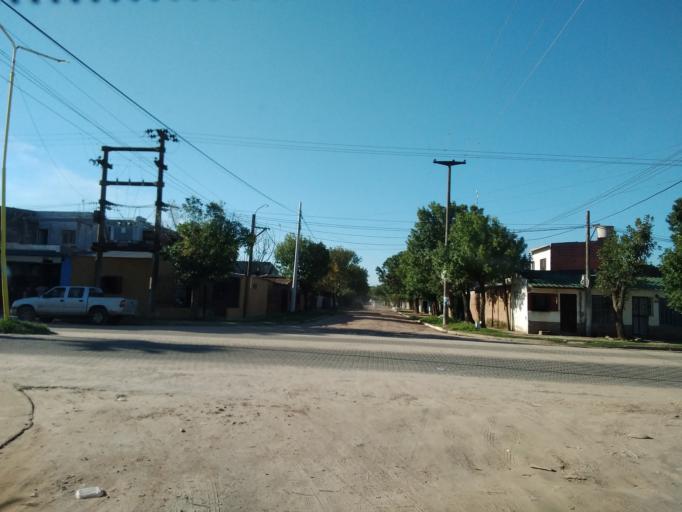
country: AR
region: Corrientes
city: Corrientes
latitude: -27.5065
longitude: -58.7801
